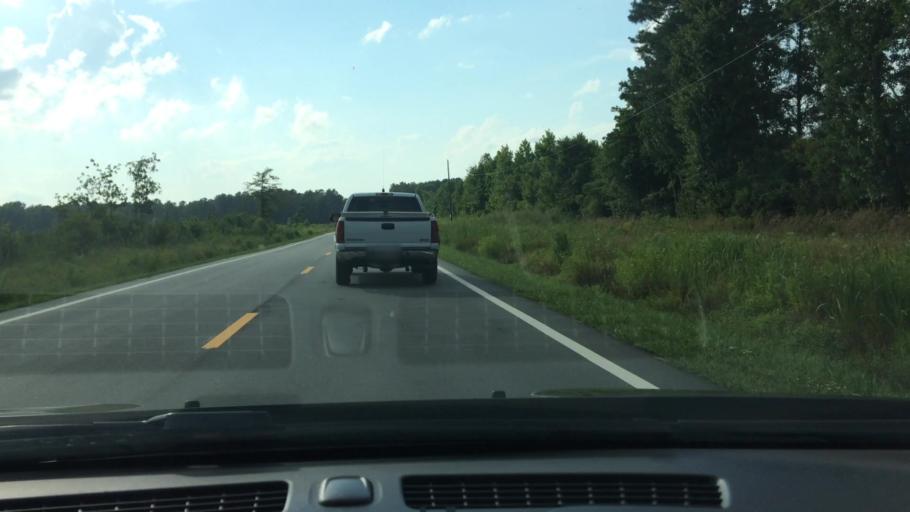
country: US
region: North Carolina
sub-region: Craven County
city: Vanceboro
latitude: 35.4349
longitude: -77.1374
